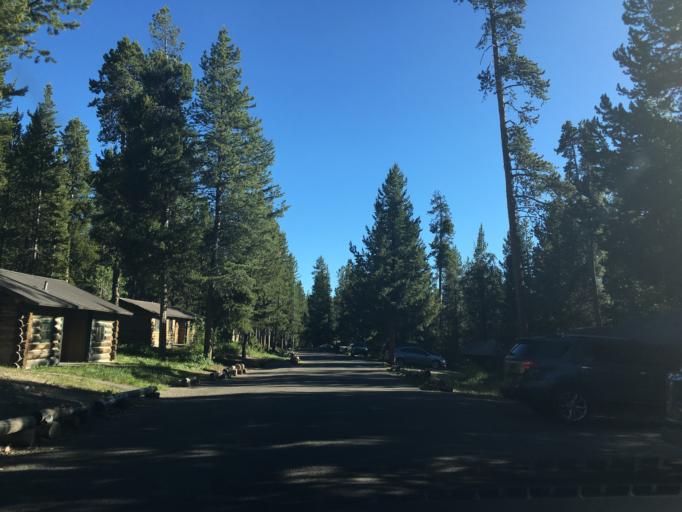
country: US
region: Wyoming
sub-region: Teton County
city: Moose Wilson Road
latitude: 43.9038
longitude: -110.6401
